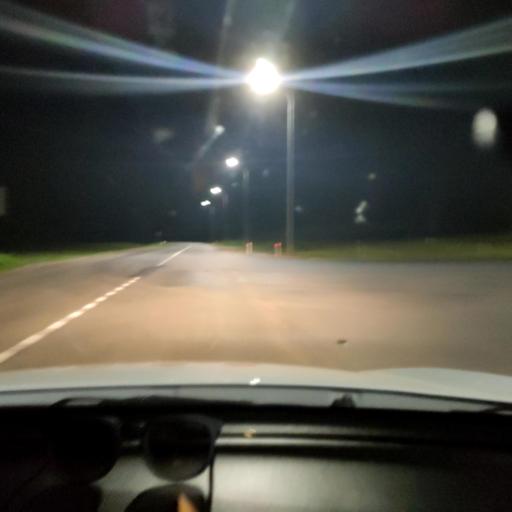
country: RU
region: Tatarstan
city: Rybnaya Sloboda
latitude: 55.4829
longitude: 50.1201
